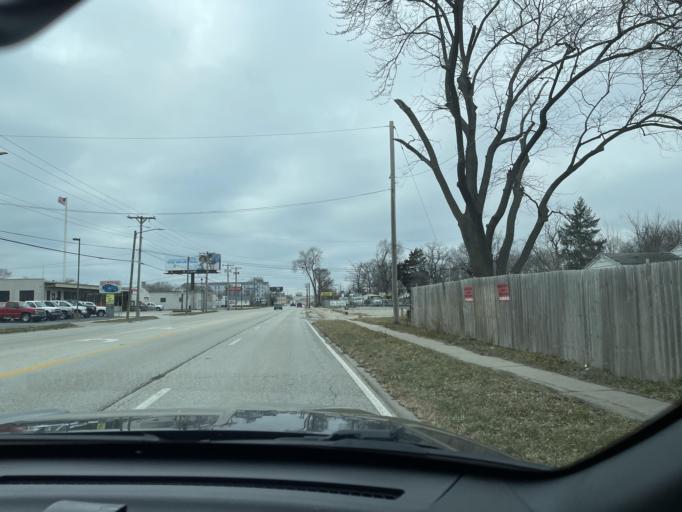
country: US
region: Illinois
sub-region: Sangamon County
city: Grandview
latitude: 39.8020
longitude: -89.6214
